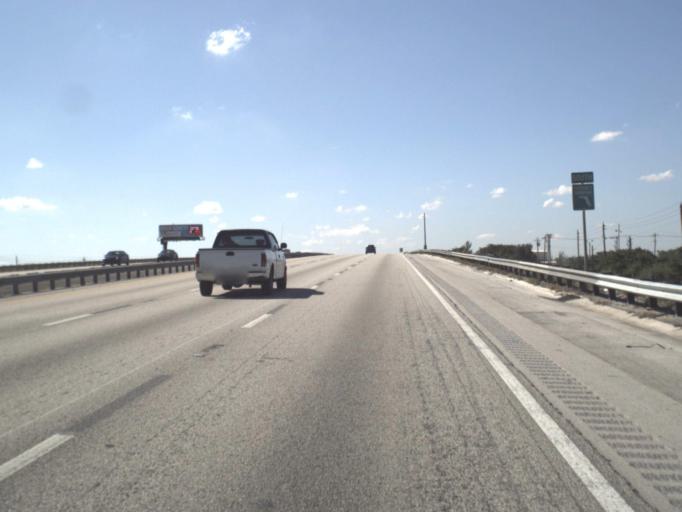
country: US
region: Florida
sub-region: Miami-Dade County
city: Palm Springs North
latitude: 25.8963
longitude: -80.3872
